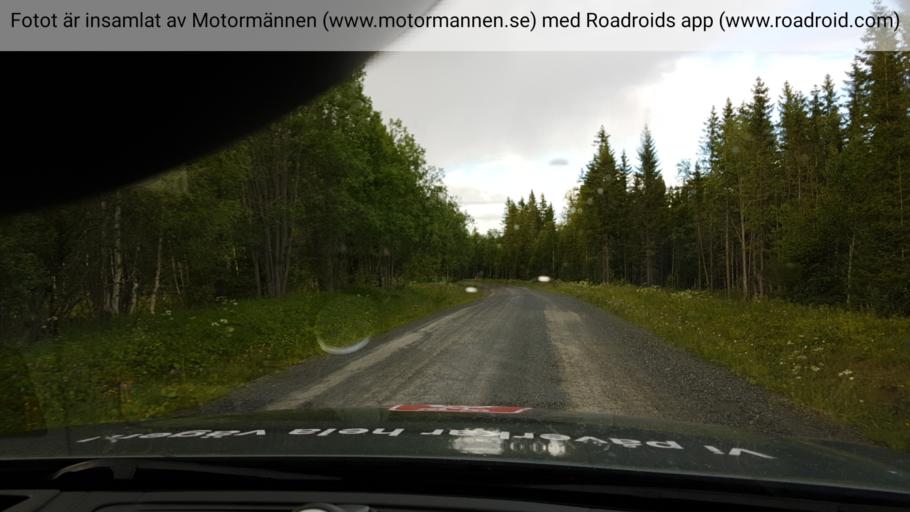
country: SE
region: Jaemtland
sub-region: Bergs Kommun
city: Hoverberg
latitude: 62.9622
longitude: 14.2363
